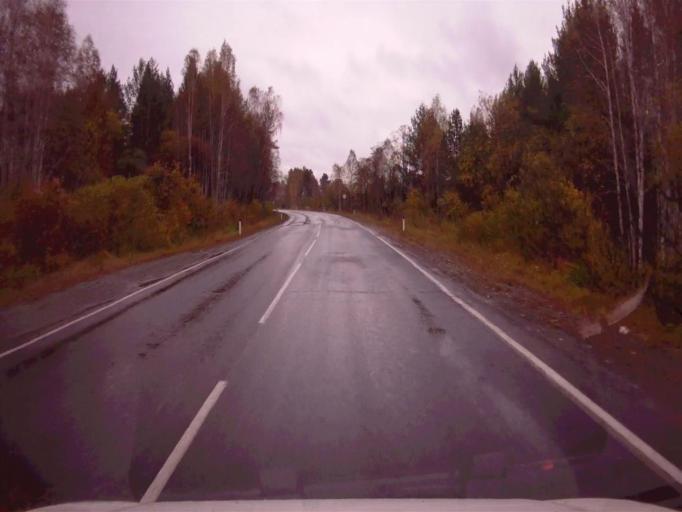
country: RU
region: Chelyabinsk
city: Verkhniy Ufaley
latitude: 55.9945
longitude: 60.3326
